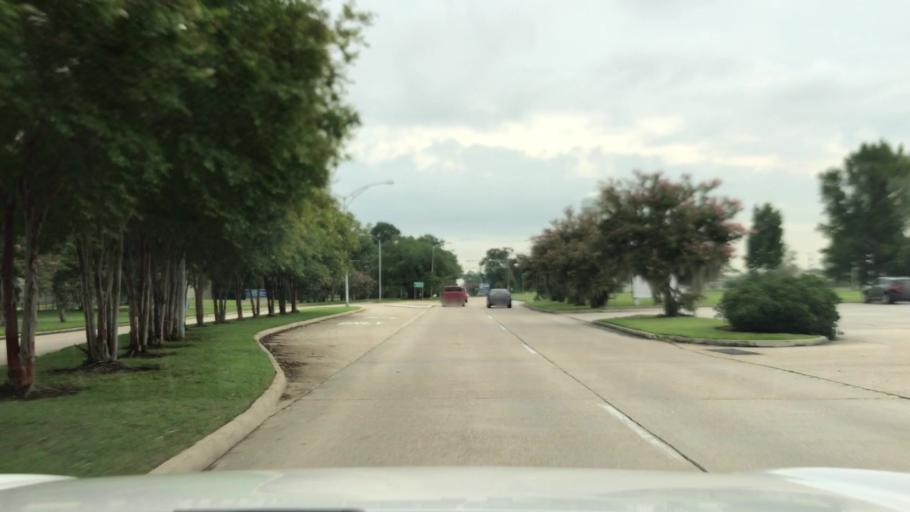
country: US
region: Louisiana
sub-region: East Baton Rouge Parish
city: Brownsfield
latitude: 30.5258
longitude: -91.1610
